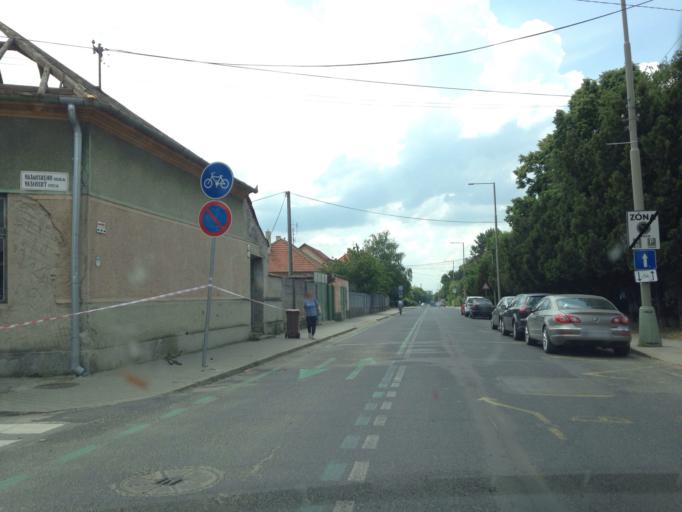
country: SK
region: Nitriansky
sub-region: Okres Nove Zamky
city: Sturovo
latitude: 47.7969
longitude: 18.7201
